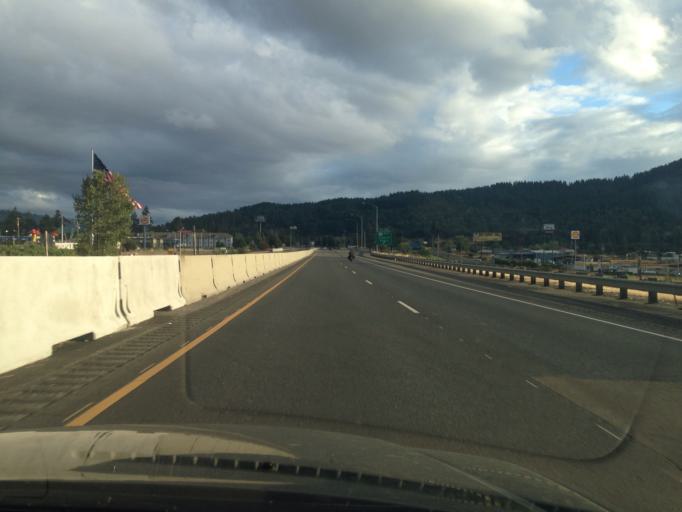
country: US
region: Oregon
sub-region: Douglas County
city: Sutherlin
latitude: 43.3885
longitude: -123.3376
